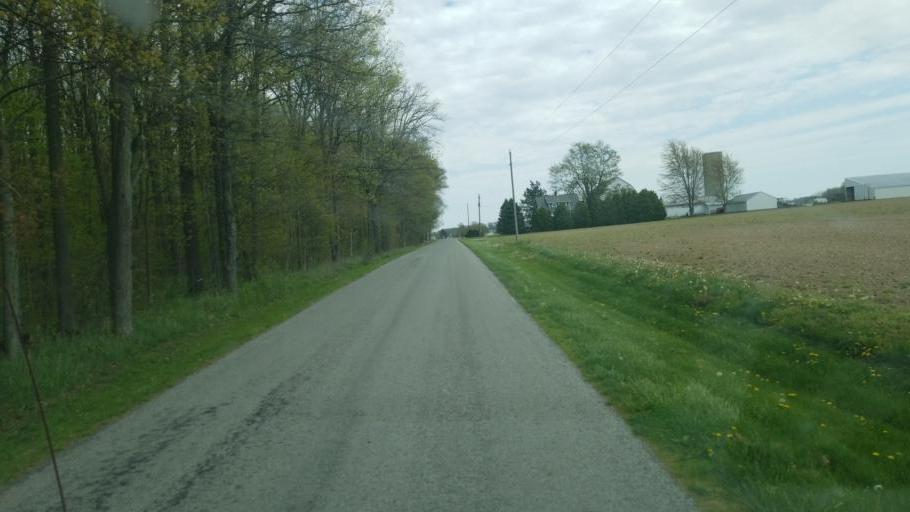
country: US
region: Ohio
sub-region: Allen County
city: Bluffton
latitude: 40.8123
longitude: -83.9039
